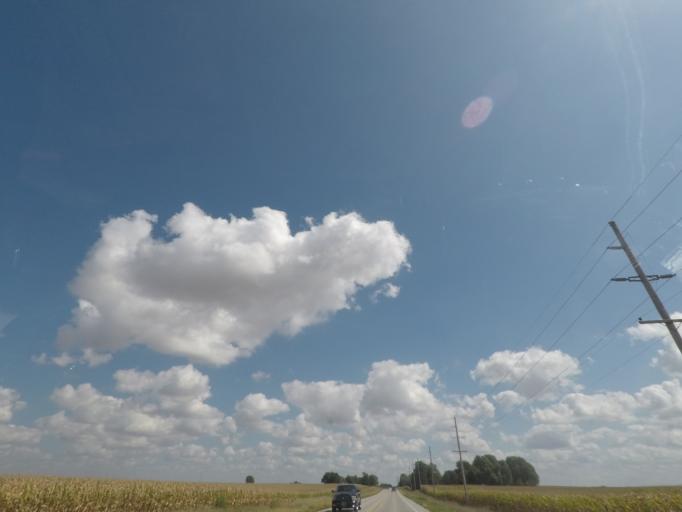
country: US
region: Iowa
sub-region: Story County
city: Nevada
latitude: 42.0227
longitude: -93.4258
